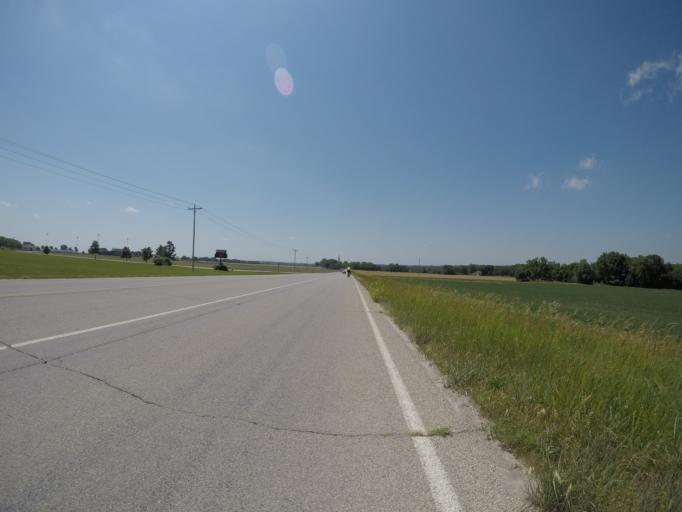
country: US
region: Kansas
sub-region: Pottawatomie County
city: Westmoreland
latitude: 39.3021
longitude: -96.4409
